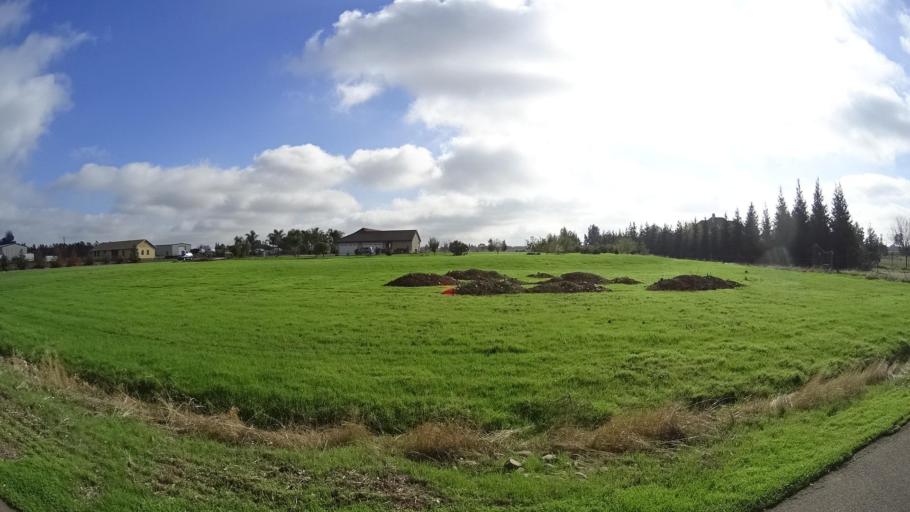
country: US
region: California
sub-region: Sacramento County
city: Vineyard
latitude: 38.4345
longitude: -121.3414
